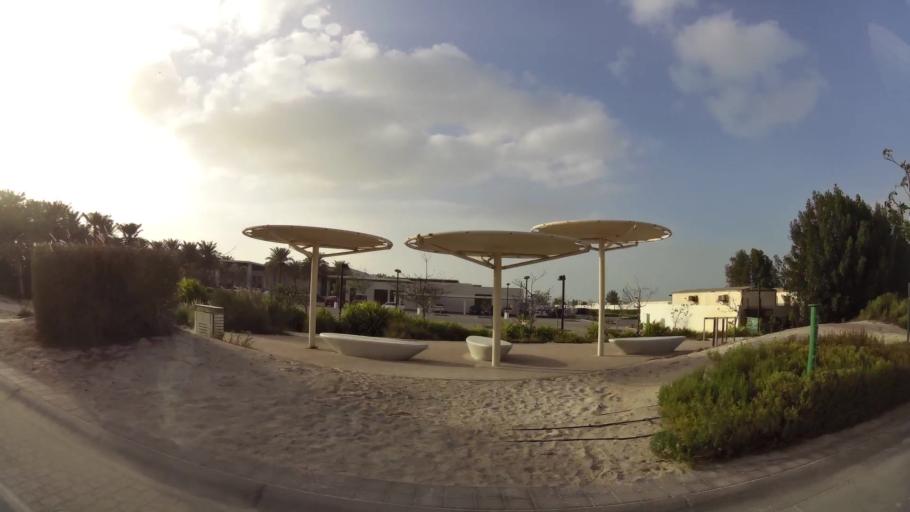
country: AE
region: Abu Dhabi
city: Abu Dhabi
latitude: 24.5578
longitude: 54.4511
